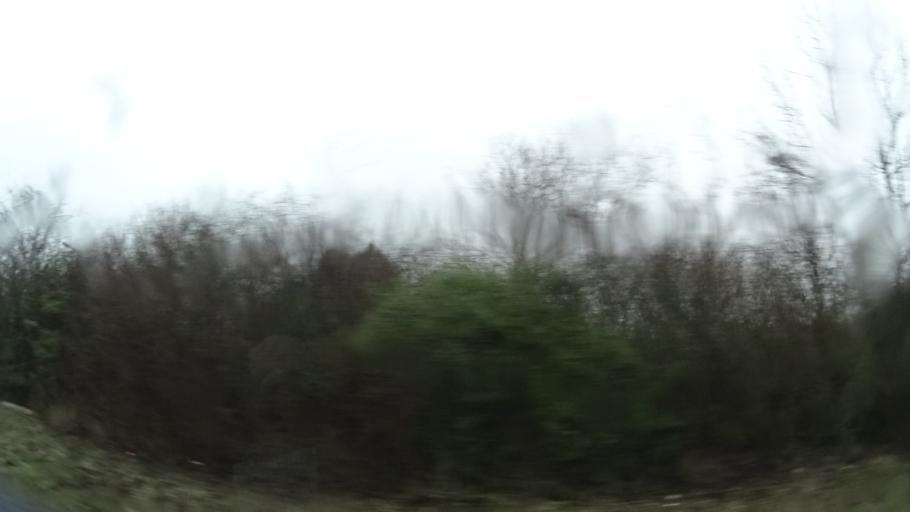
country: DE
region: Thuringia
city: Eisfeld
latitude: 50.4426
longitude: 10.9107
